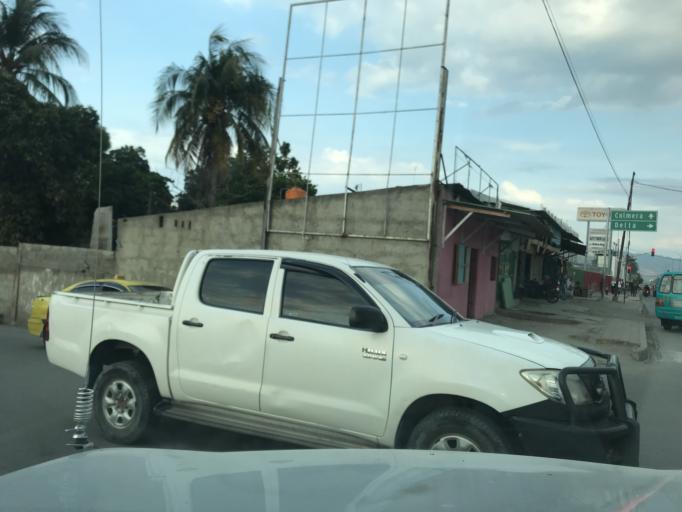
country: TL
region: Dili
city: Dili
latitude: -8.5542
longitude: 125.5397
